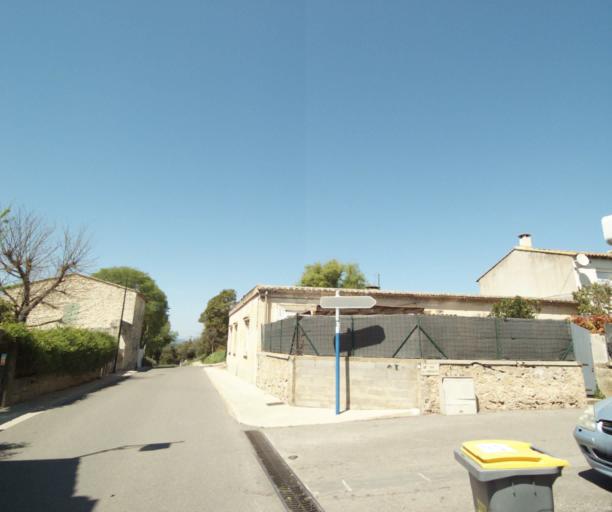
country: FR
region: Languedoc-Roussillon
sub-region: Departement de l'Herault
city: Beaulieu
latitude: 43.7299
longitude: 4.0193
